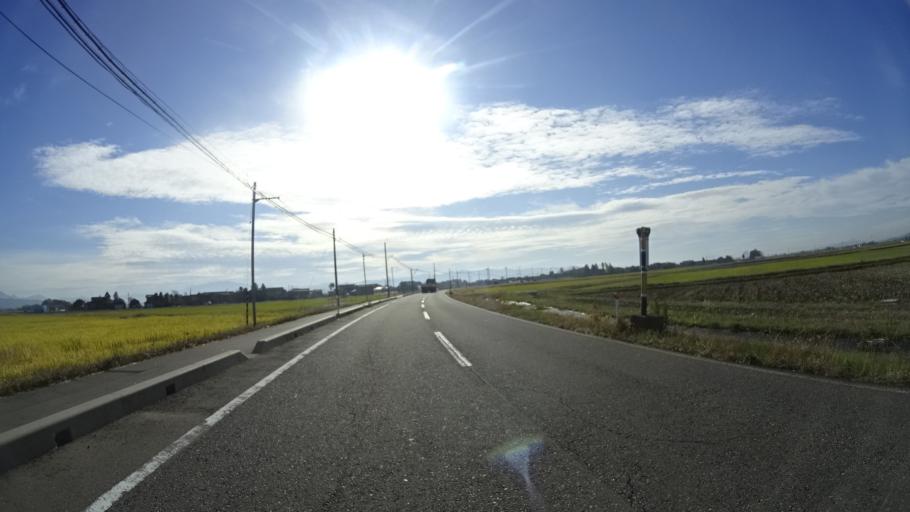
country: JP
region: Niigata
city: Mitsuke
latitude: 37.5639
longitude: 138.8484
